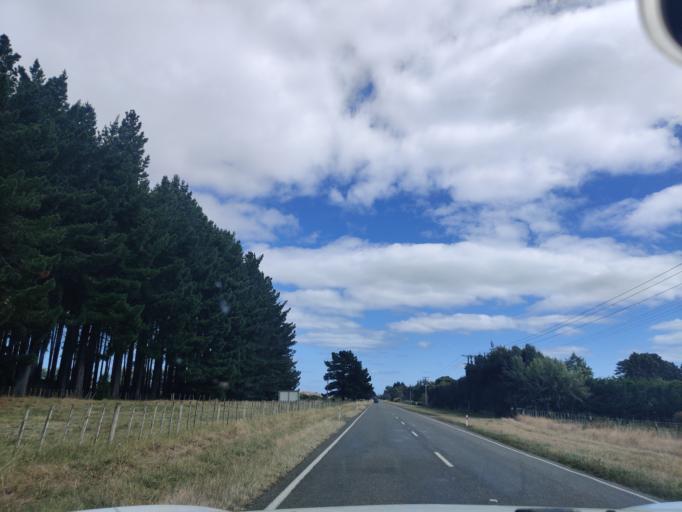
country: NZ
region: Manawatu-Wanganui
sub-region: Horowhenua District
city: Foxton
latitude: -40.3983
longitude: 175.3475
